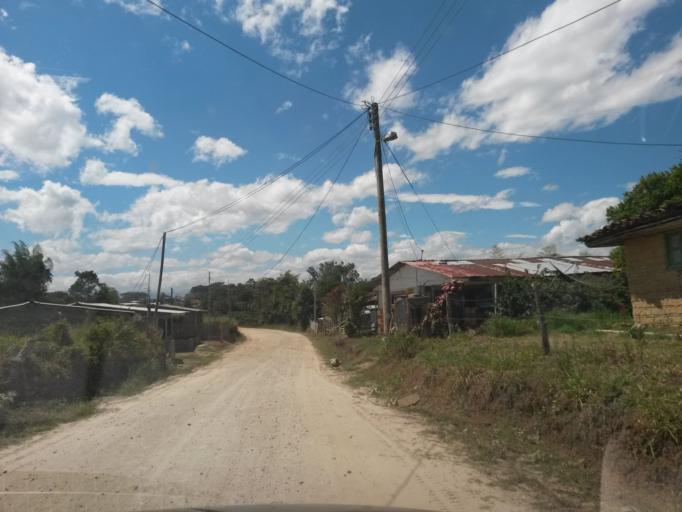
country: CO
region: Cauca
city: Morales
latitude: 2.7469
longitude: -76.6295
